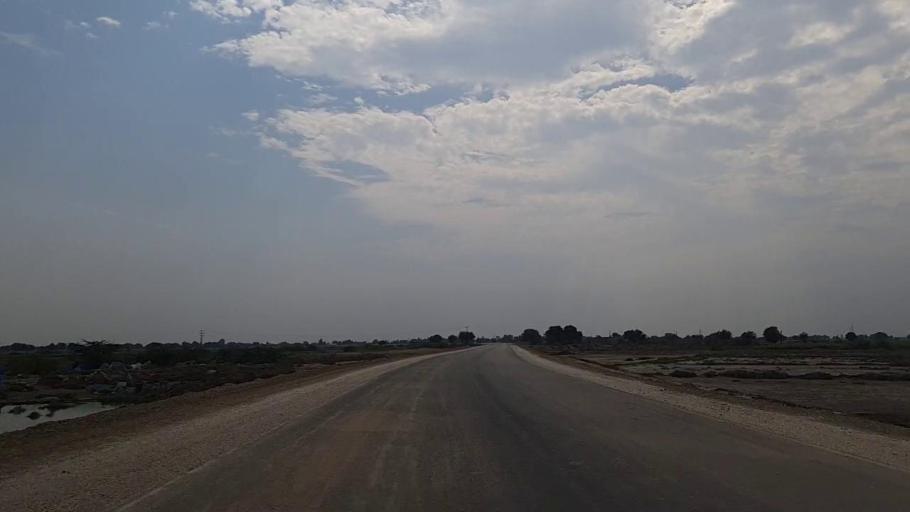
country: PK
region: Sindh
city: Naukot
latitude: 24.9884
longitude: 69.2851
